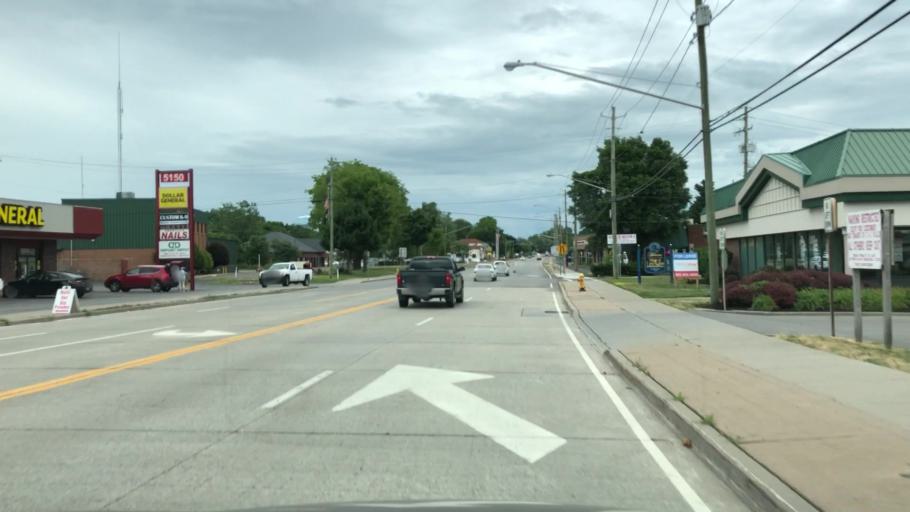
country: US
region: New York
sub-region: Erie County
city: Depew
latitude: 42.9013
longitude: -78.6836
